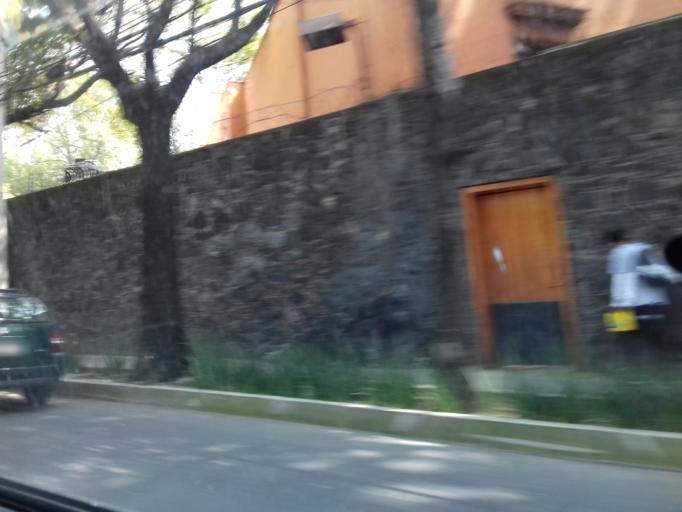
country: MX
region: Mexico City
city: Coyoacan
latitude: 19.3484
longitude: -99.1803
